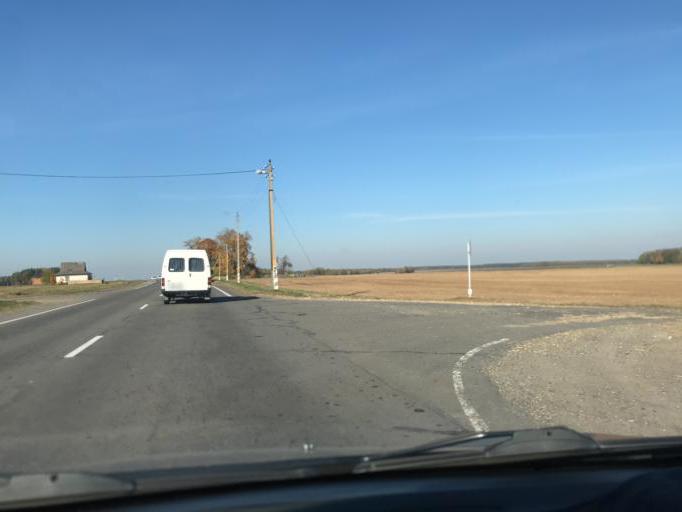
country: BY
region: Gomel
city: Parychy
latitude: 52.6520
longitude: 29.3692
